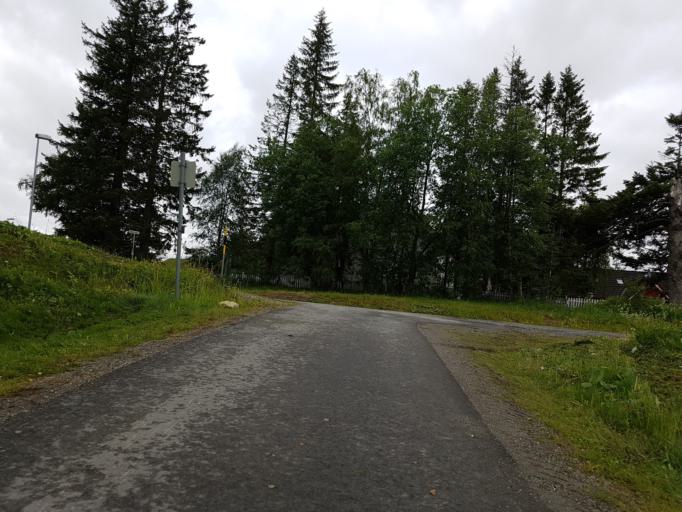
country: NO
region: Sor-Trondelag
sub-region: Selbu
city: Mebonden
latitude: 63.2213
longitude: 11.0297
